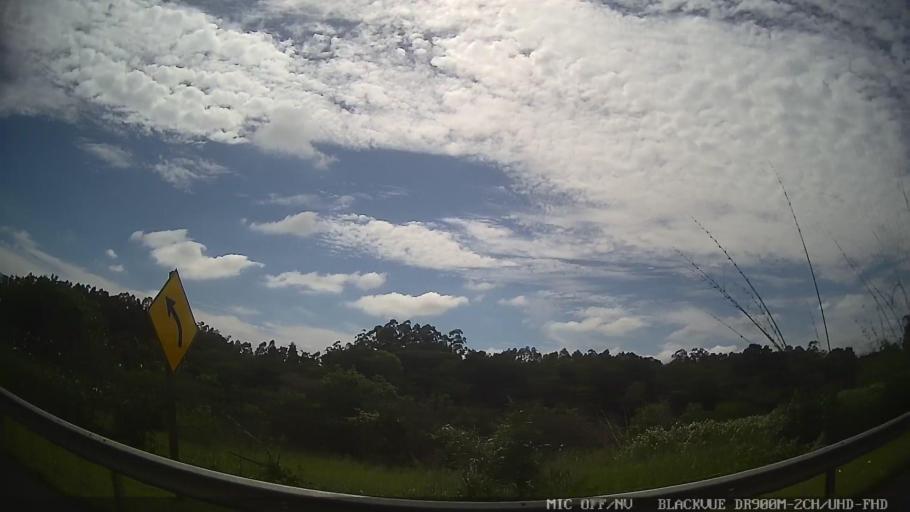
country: BR
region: Sao Paulo
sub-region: Laranjal Paulista
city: Laranjal Paulista
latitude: -23.0543
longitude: -47.8226
